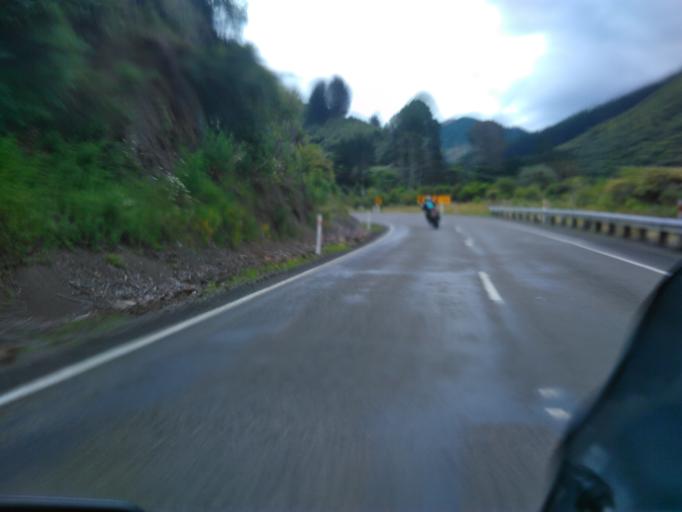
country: NZ
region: Bay of Plenty
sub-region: Opotiki District
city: Opotiki
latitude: -38.2541
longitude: 177.2995
